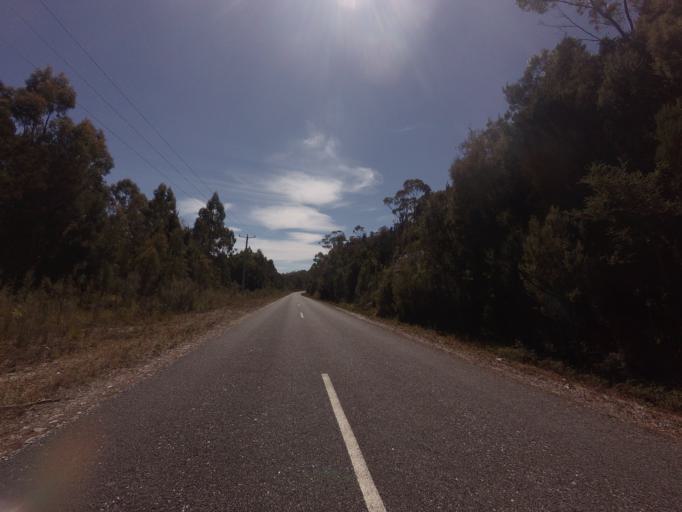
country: AU
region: Tasmania
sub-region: West Coast
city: Queenstown
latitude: -42.7797
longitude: 146.0297
